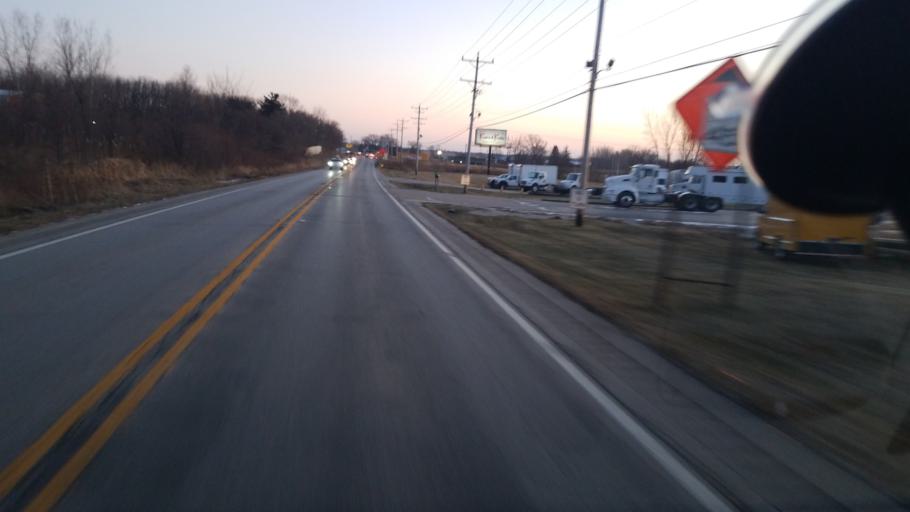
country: US
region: Illinois
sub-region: Kane County
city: Hampshire
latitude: 42.1668
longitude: -88.5292
